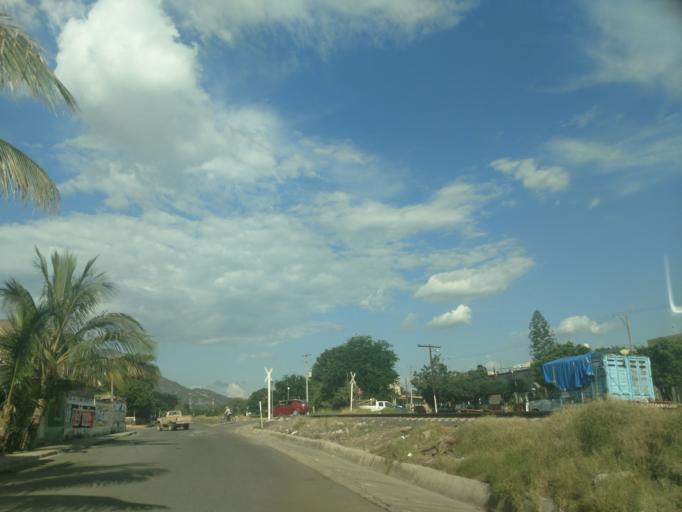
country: MX
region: Jalisco
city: Antonio Escobedo
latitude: 20.9068
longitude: -103.9774
